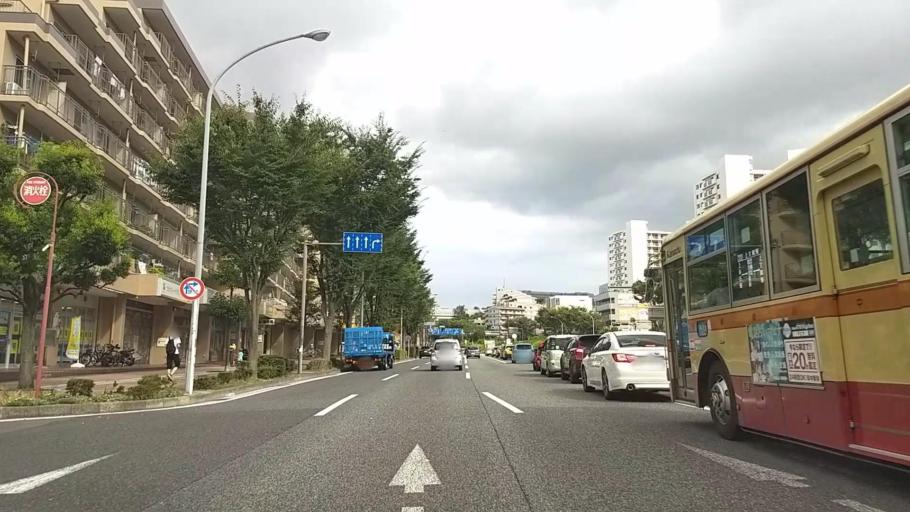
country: JP
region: Kanagawa
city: Yokohama
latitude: 35.4038
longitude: 139.5715
